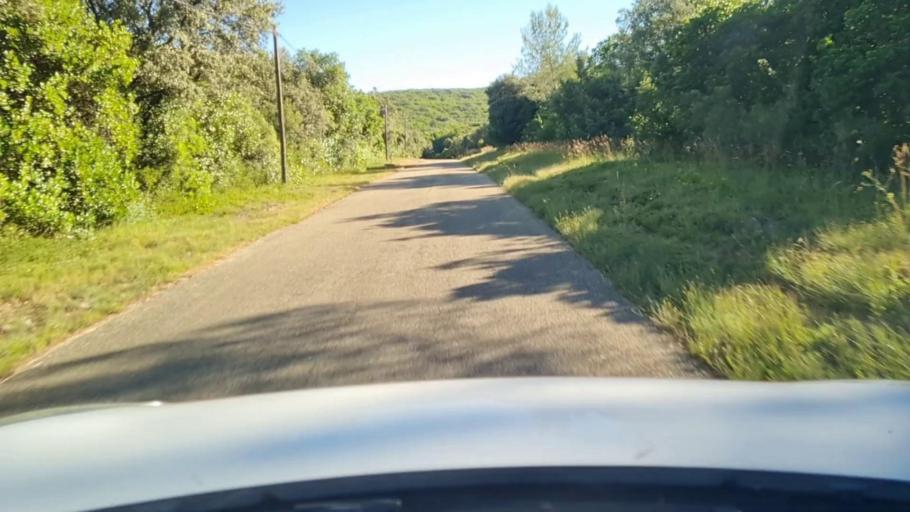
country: FR
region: Languedoc-Roussillon
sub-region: Departement du Gard
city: Villevieille
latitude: 43.8467
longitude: 4.0793
